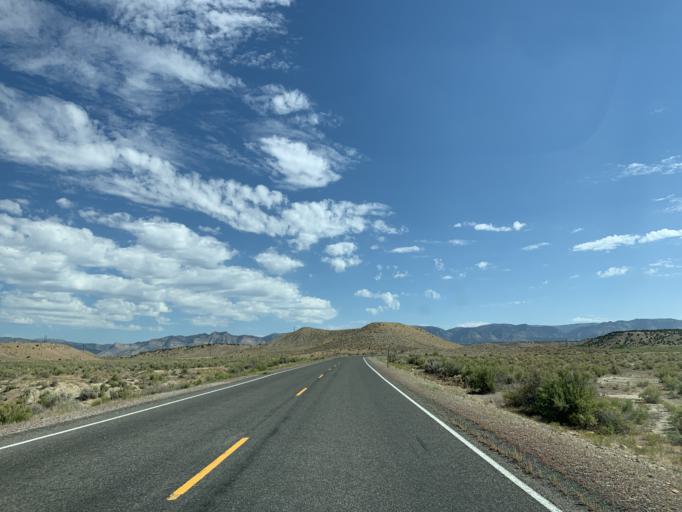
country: US
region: Utah
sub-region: Carbon County
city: Wellington
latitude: 39.5783
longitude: -110.6519
